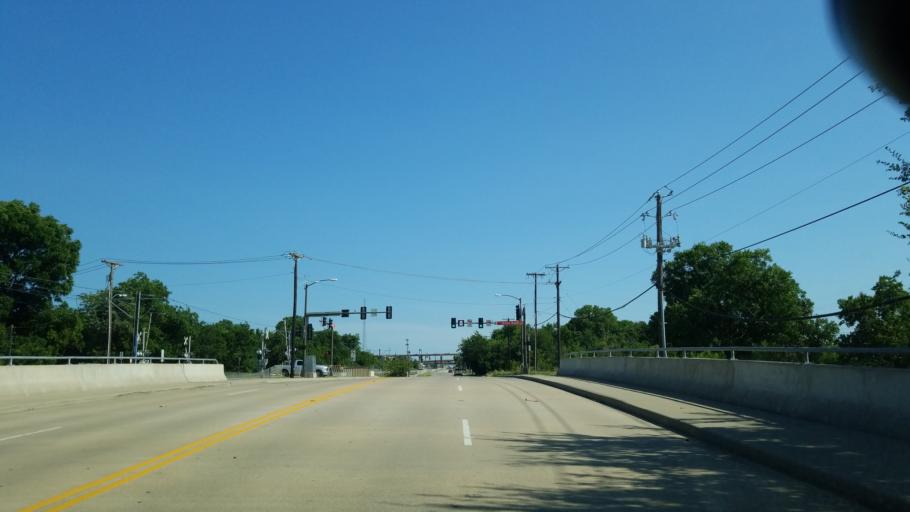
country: US
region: Texas
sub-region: Dallas County
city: Farmers Branch
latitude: 32.9186
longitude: -96.8955
